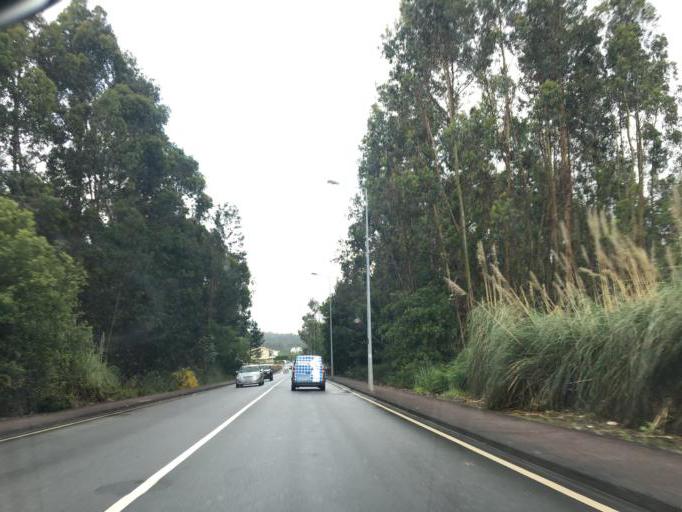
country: PT
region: Porto
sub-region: Maia
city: Nogueira
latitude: 41.2558
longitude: -8.5956
